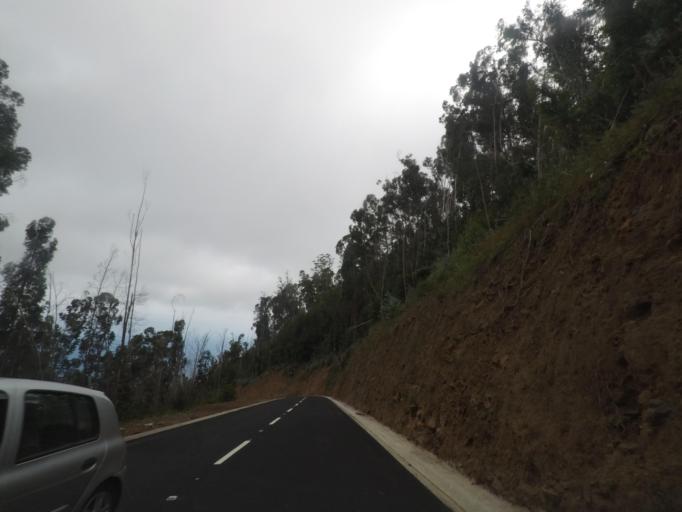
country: PT
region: Madeira
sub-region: Calheta
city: Estreito da Calheta
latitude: 32.7481
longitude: -17.1570
